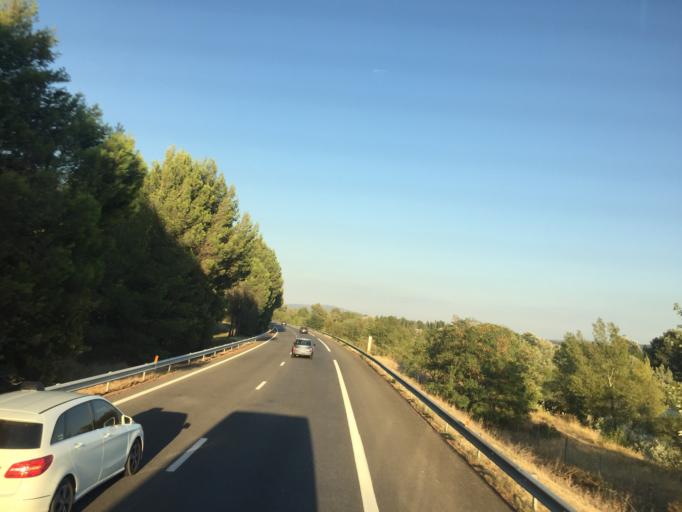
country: FR
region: Provence-Alpes-Cote d'Azur
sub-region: Departement des Bouches-du-Rhone
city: Meyrargues
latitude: 43.6567
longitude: 5.5257
